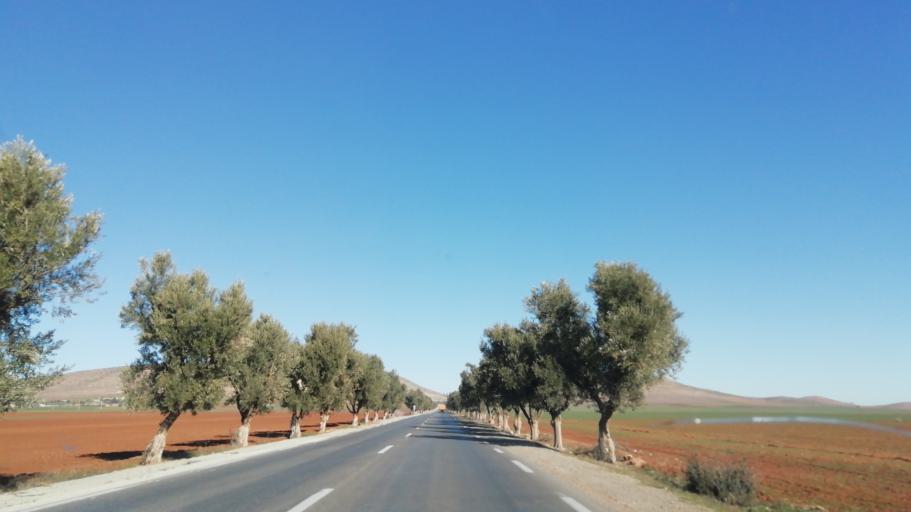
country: DZ
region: Mascara
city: Mascara
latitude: 35.2226
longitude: 0.1136
